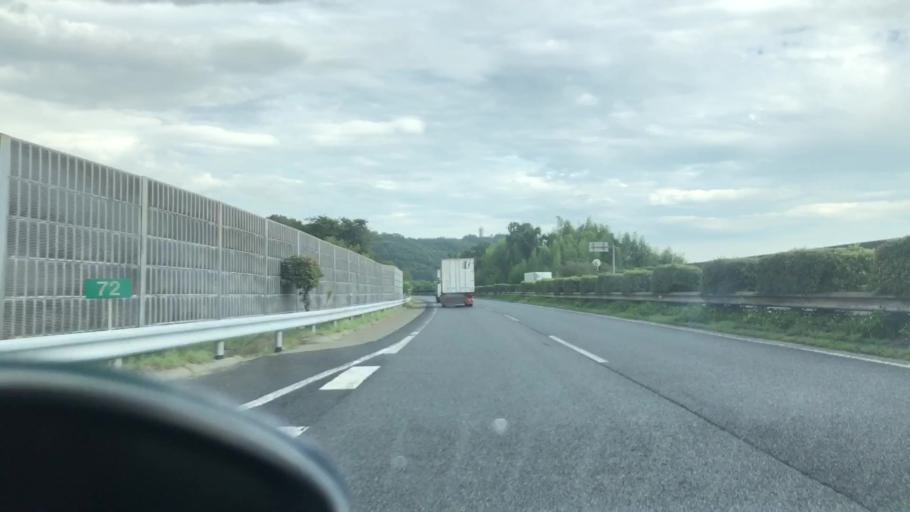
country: JP
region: Hyogo
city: Ono
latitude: 34.9344
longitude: 134.8389
